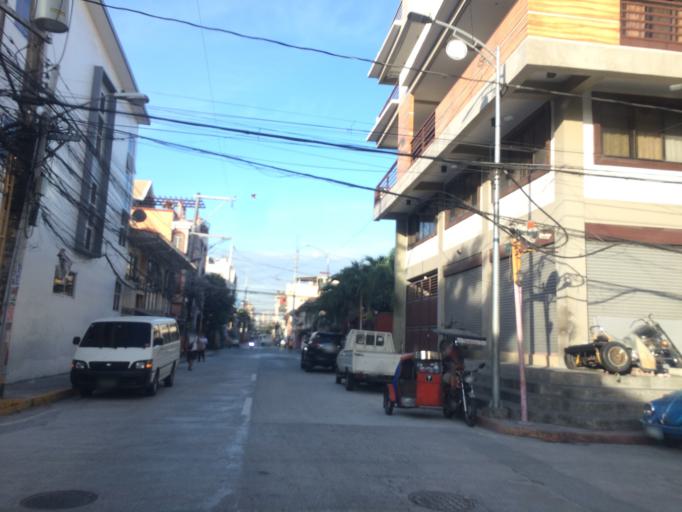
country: PH
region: Metro Manila
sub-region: City of Manila
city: Manila
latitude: 14.6212
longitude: 120.9945
